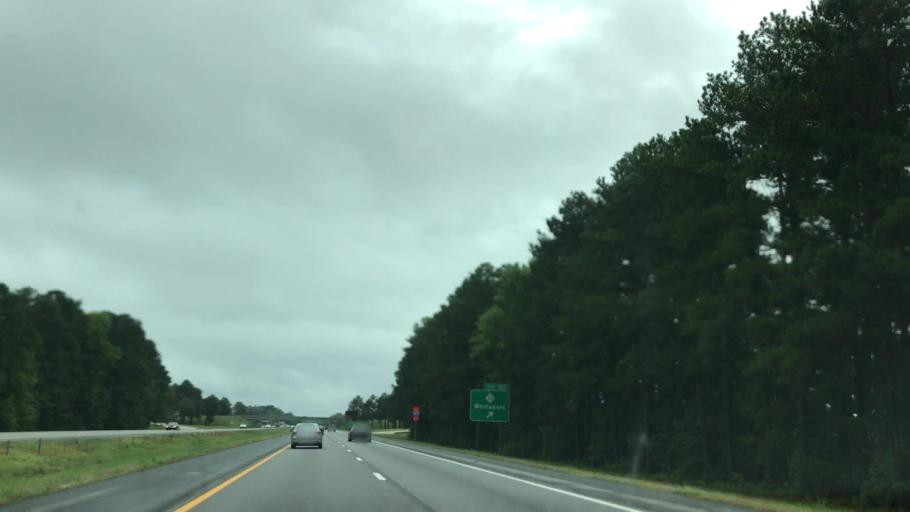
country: US
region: North Carolina
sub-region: Nash County
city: Red Oak
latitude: 36.1227
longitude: -77.7979
